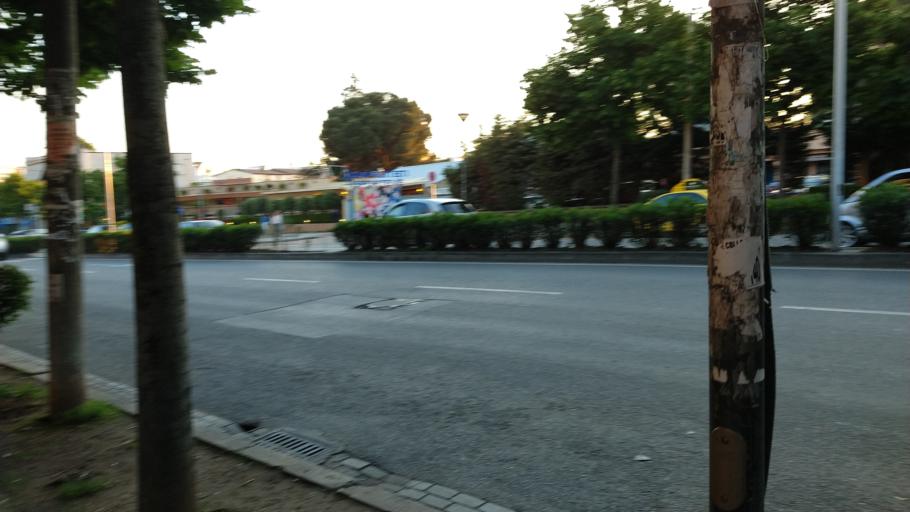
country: AL
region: Tirane
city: Tirana
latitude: 41.3306
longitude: 19.8036
